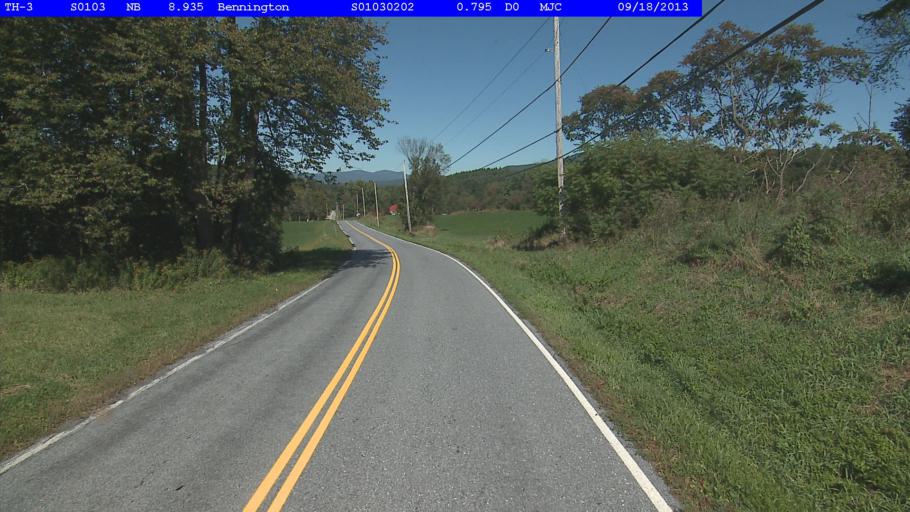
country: US
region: Vermont
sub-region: Bennington County
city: Bennington
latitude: 42.8481
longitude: -73.1721
